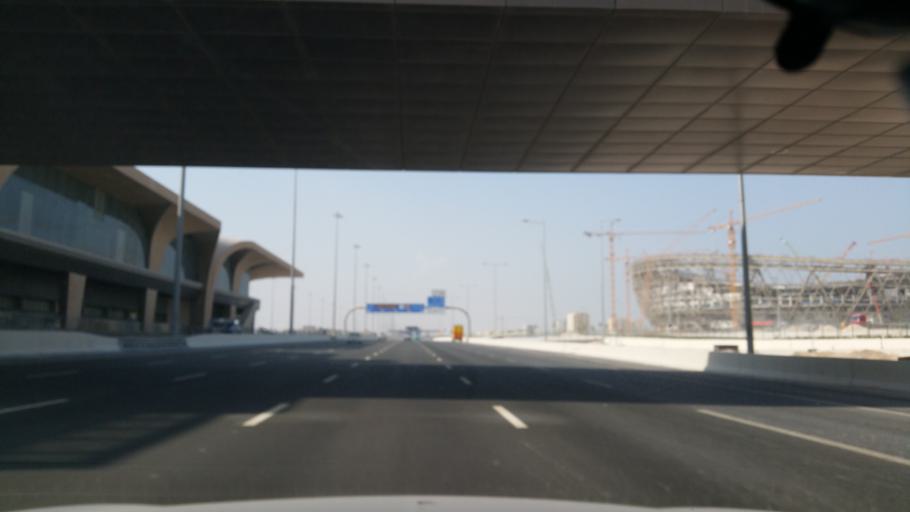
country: QA
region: Baladiyat Umm Salal
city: Umm Salal Muhammad
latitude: 25.4145
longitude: 51.4883
